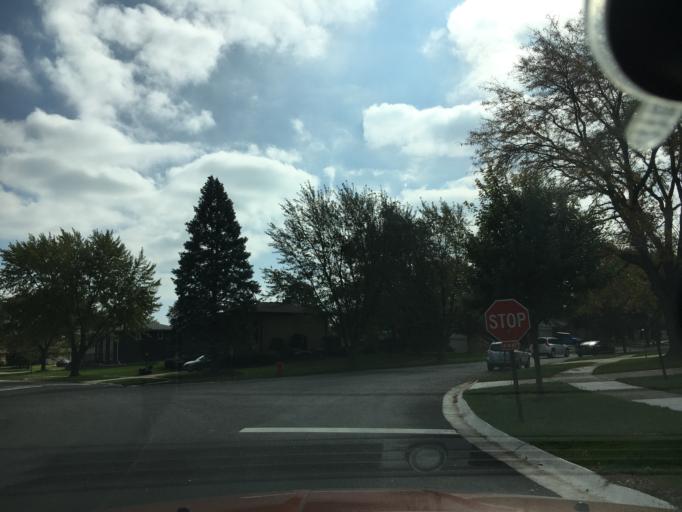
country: US
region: Illinois
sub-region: Cook County
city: Tinley Park
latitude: 41.6114
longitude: -87.7834
